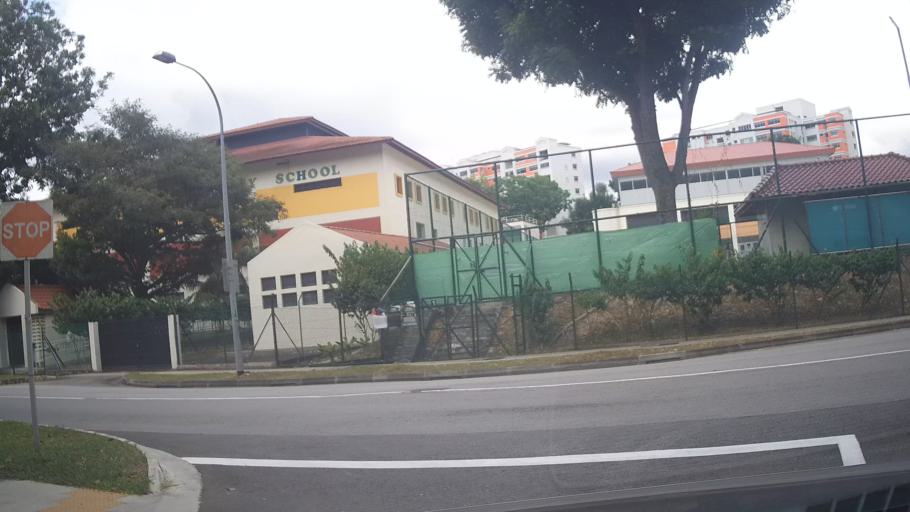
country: MY
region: Johor
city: Johor Bahru
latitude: 1.4412
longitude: 103.7949
